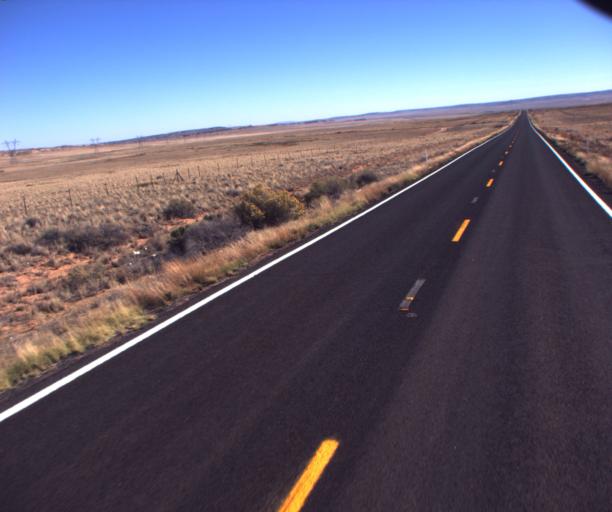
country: US
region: Arizona
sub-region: Coconino County
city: Tuba City
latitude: 35.9714
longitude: -110.8339
